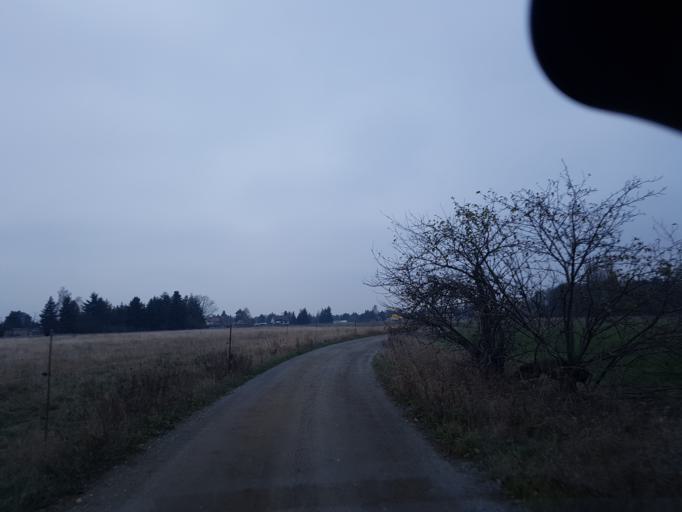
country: DE
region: Brandenburg
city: Finsterwalde
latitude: 51.6180
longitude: 13.7313
